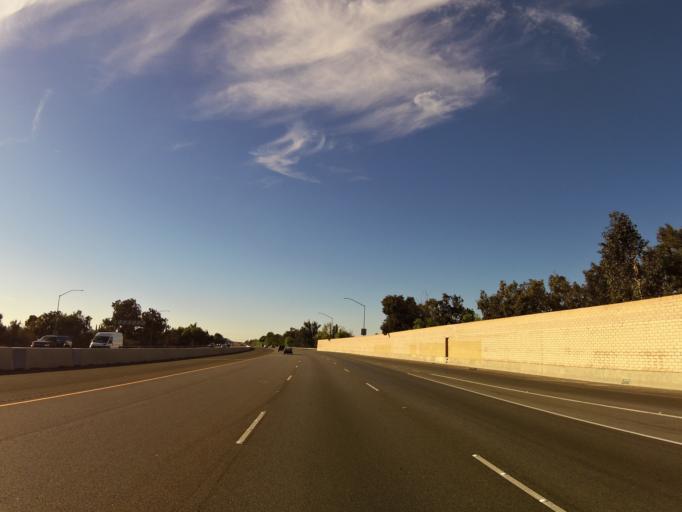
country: US
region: California
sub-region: Ventura County
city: Santa Susana
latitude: 34.2822
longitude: -118.7205
